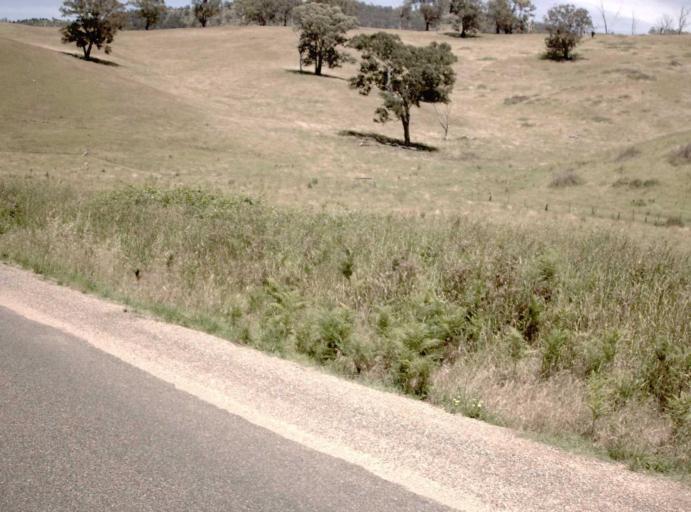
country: AU
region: Victoria
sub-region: East Gippsland
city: Bairnsdale
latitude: -37.4036
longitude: 147.8347
